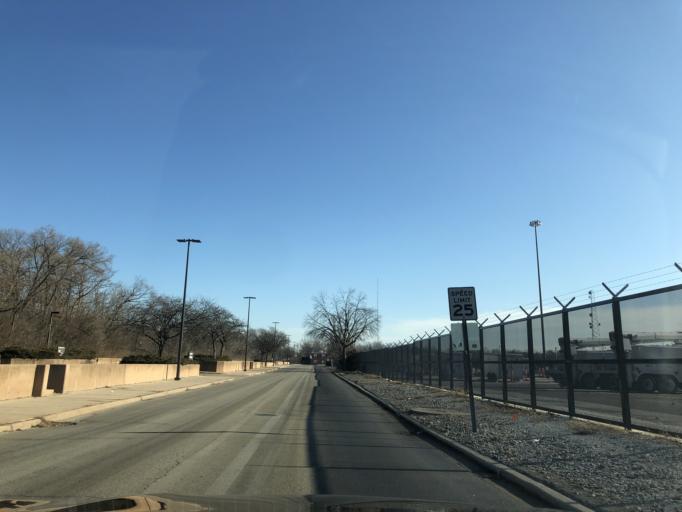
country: US
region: Illinois
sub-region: Cook County
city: Maywood
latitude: 41.8752
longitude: -87.8304
